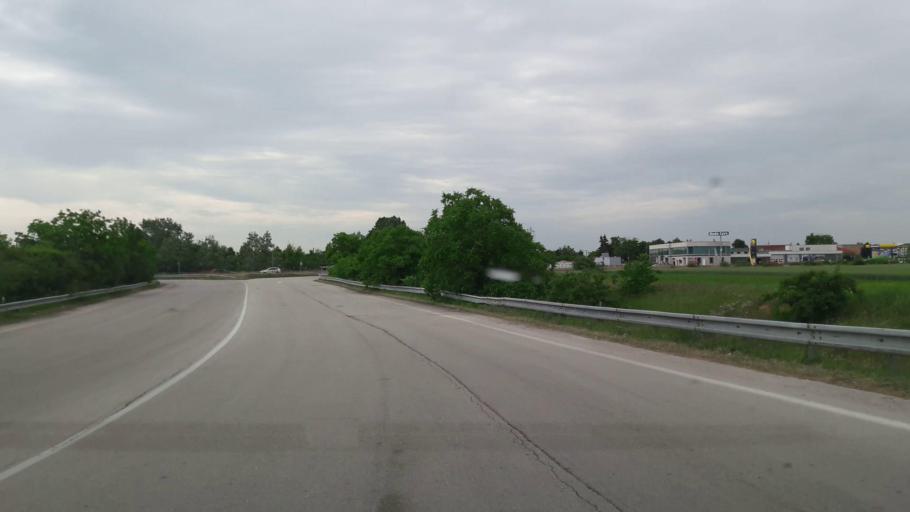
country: SK
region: Bratislavsky
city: Senec
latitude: 48.2157
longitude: 17.3837
